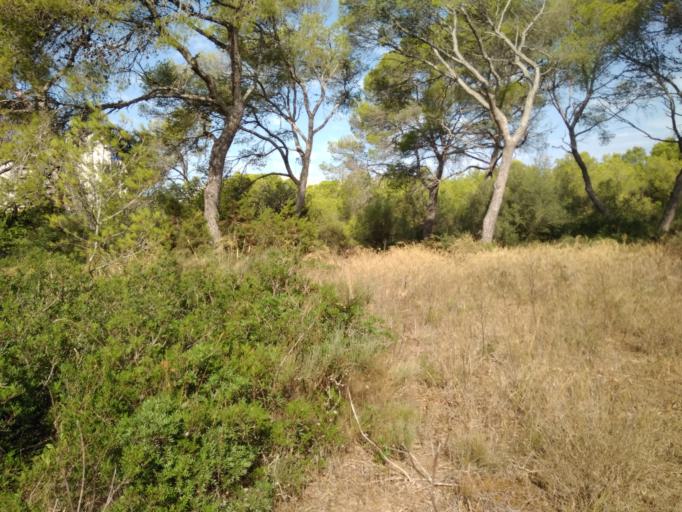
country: ES
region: Balearic Islands
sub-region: Illes Balears
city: s'Arenal
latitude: 39.5182
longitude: 2.7510
